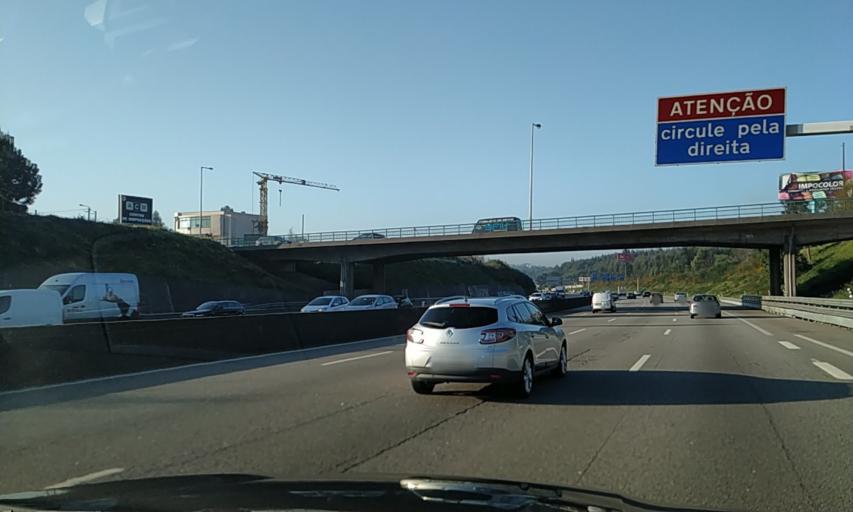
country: PT
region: Porto
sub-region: Valongo
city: Ermesinde
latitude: 41.2298
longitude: -8.5700
